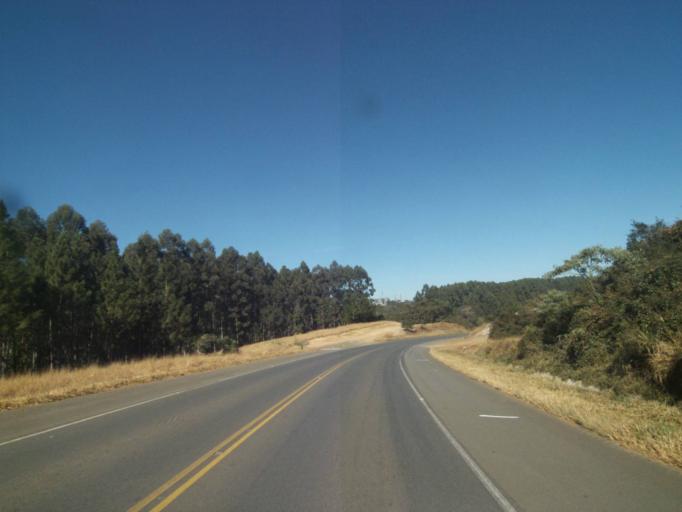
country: BR
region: Parana
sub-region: Tibagi
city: Tibagi
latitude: -24.5171
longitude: -50.4361
